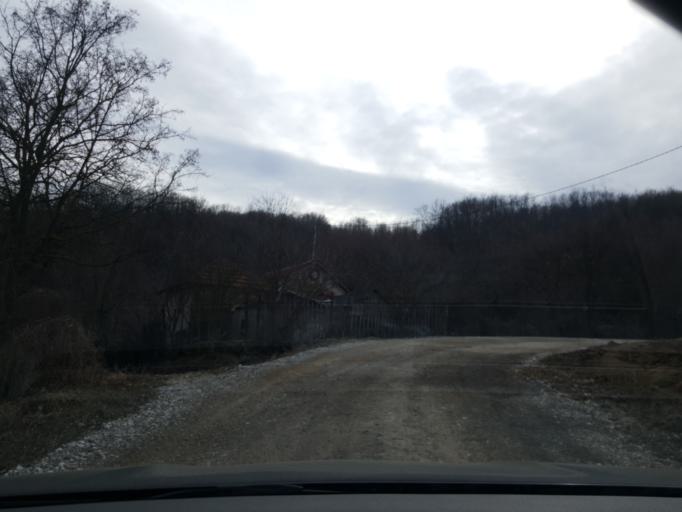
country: RS
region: Central Serbia
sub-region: Pirotski Okrug
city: Dimitrovgrad
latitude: 43.0040
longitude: 22.7528
